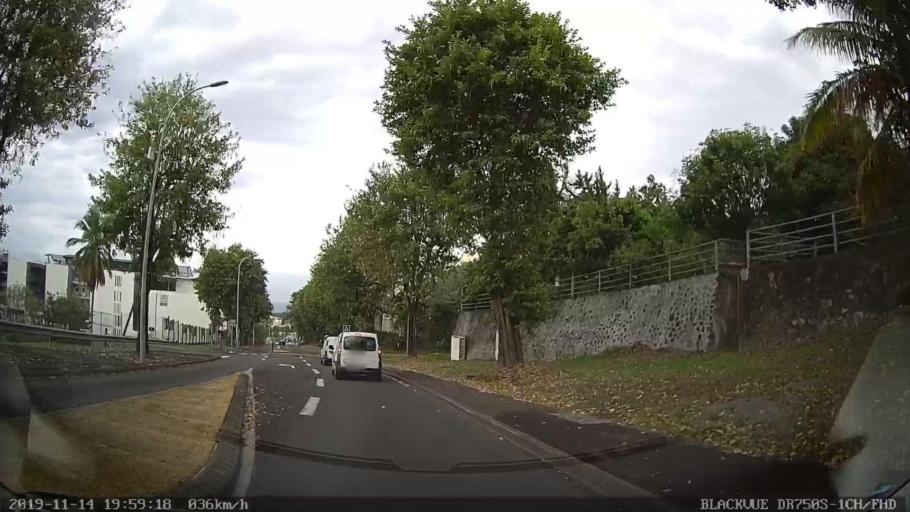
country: RE
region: Reunion
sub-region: Reunion
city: Saint-Denis
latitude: -20.9050
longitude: 55.4874
